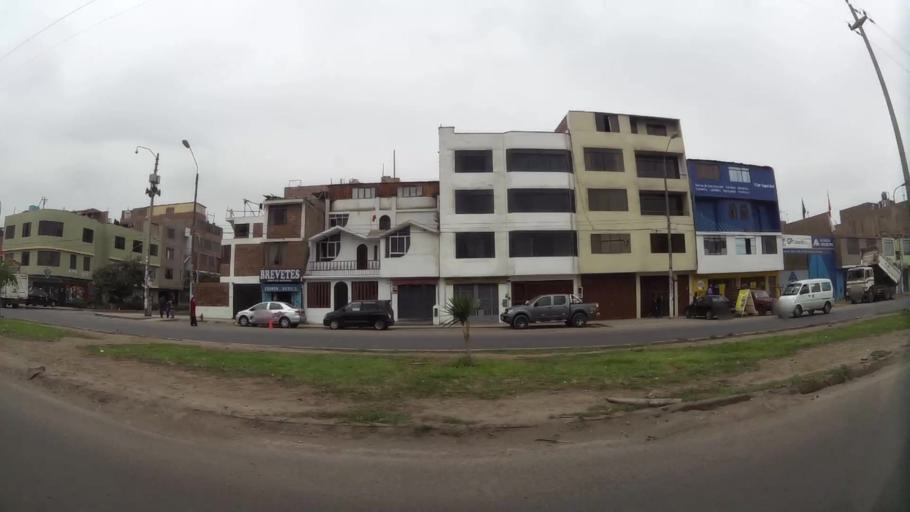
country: PE
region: Lima
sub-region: Lima
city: Independencia
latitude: -11.9795
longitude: -77.0846
